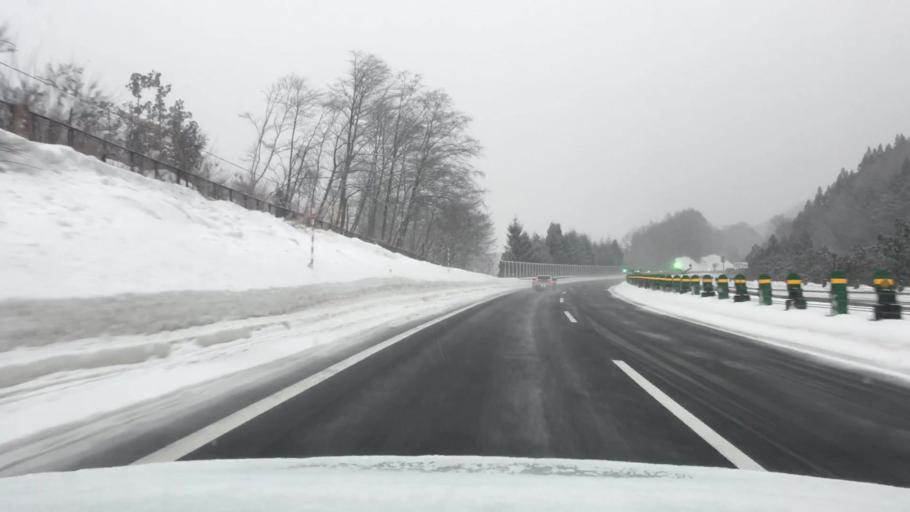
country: JP
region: Akita
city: Hanawa
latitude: 40.1335
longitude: 140.9789
